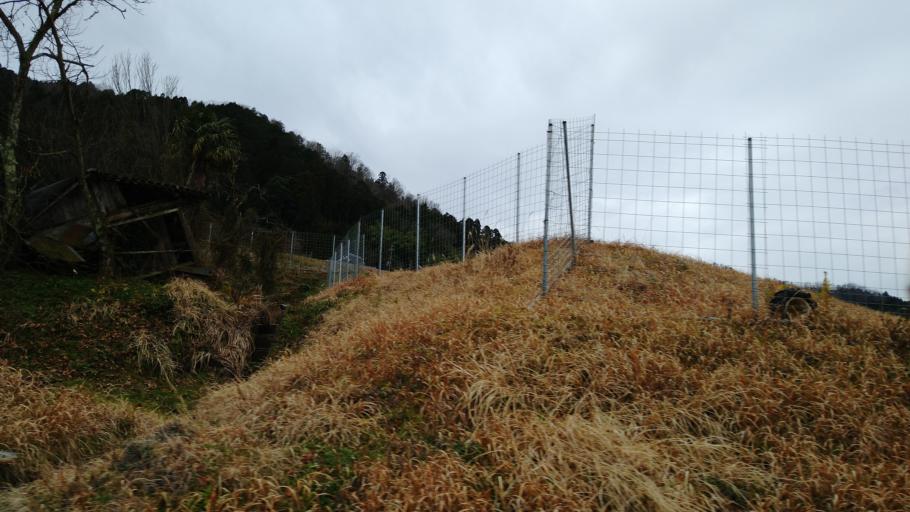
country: JP
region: Kyoto
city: Ayabe
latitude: 35.3222
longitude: 135.3597
